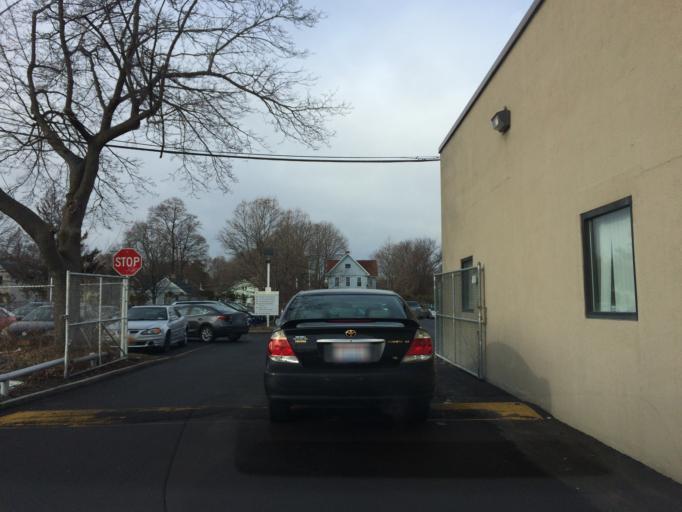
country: US
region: New York
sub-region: Monroe County
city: Rochester
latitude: 43.1419
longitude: -77.5990
